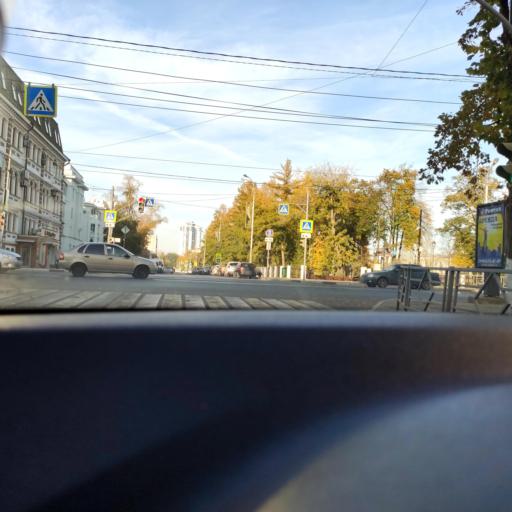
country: RU
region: Samara
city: Samara
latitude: 53.1937
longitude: 50.0986
